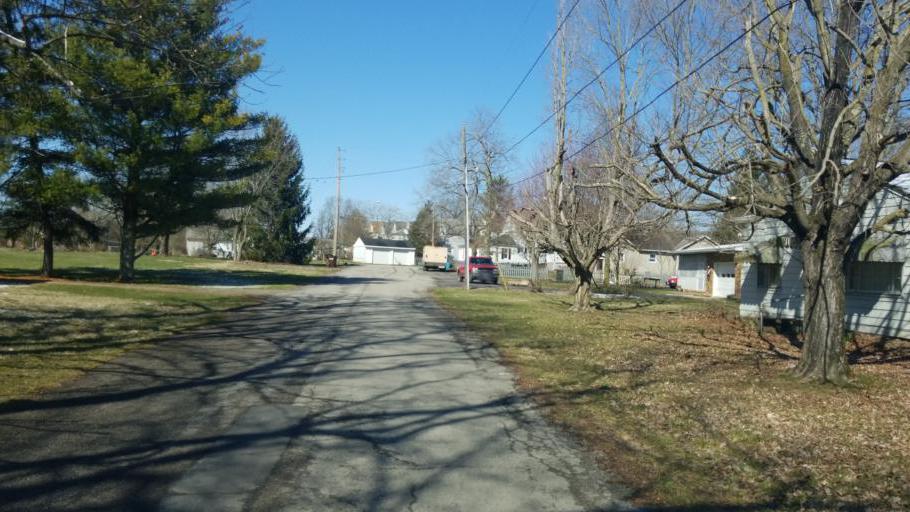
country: US
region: Ohio
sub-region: Highland County
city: Greenfield
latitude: 39.3427
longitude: -83.3823
